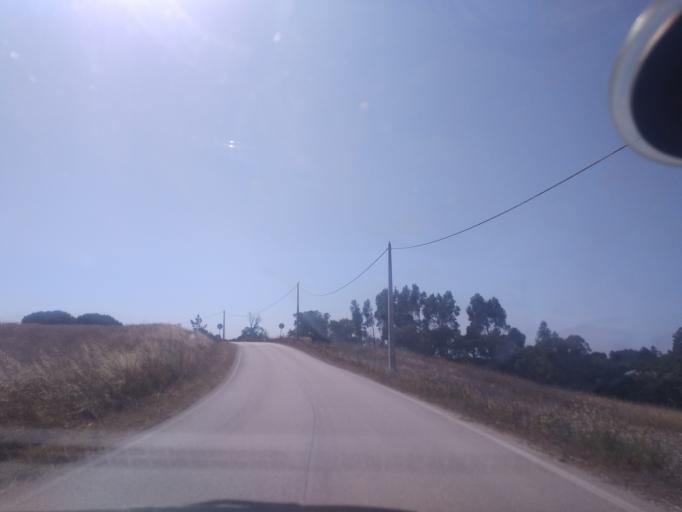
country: PT
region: Faro
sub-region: Aljezur
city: Aljezur
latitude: 37.2274
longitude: -8.8163
